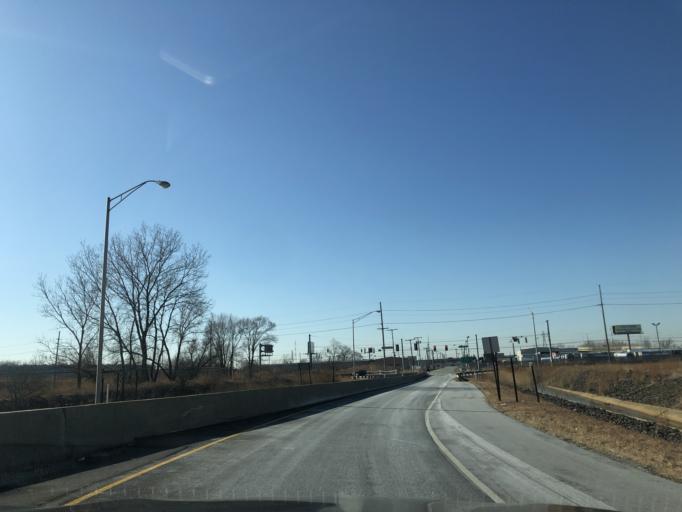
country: US
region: Indiana
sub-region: Lake County
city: Whiting
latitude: 41.6555
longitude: -87.5067
